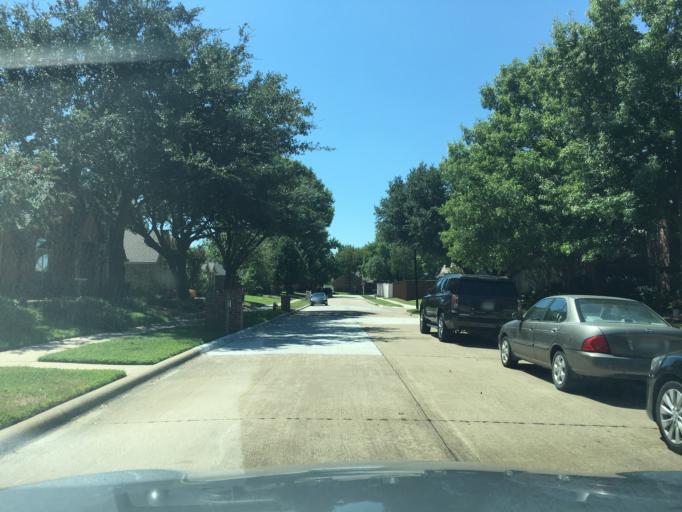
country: US
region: Texas
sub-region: Dallas County
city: Sachse
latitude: 32.9657
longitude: -96.6332
